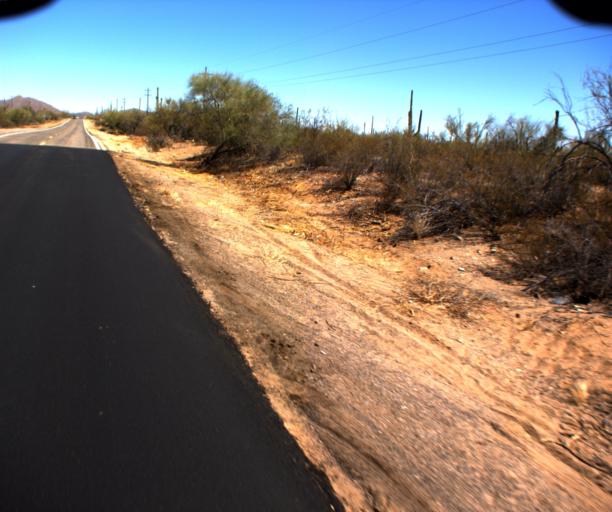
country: US
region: Arizona
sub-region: Pima County
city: Sells
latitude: 32.1435
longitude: -112.1002
